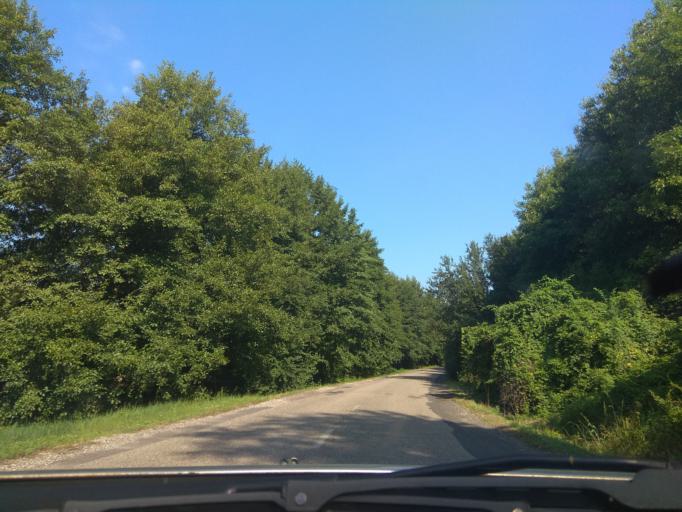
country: HU
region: Borsod-Abauj-Zemplen
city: Harsany
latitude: 47.9941
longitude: 20.7628
